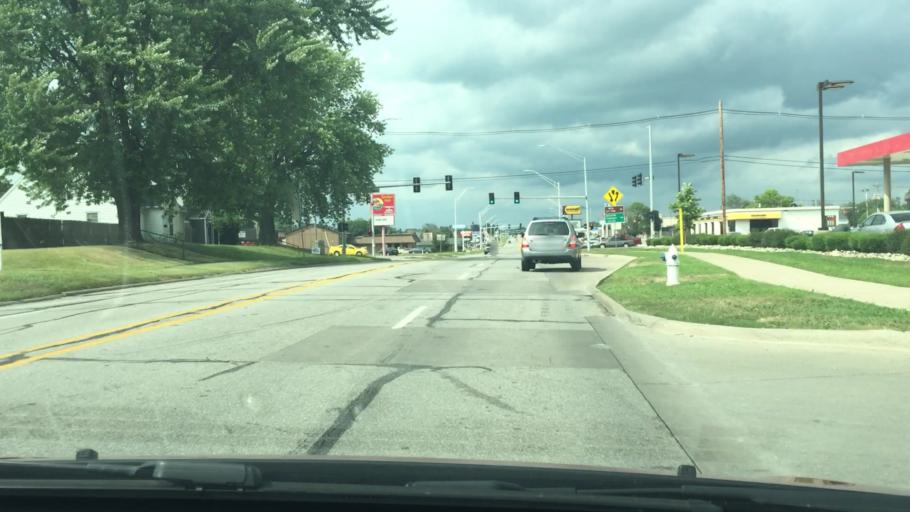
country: US
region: Iowa
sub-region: Muscatine County
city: Muscatine
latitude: 41.4414
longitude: -91.0306
